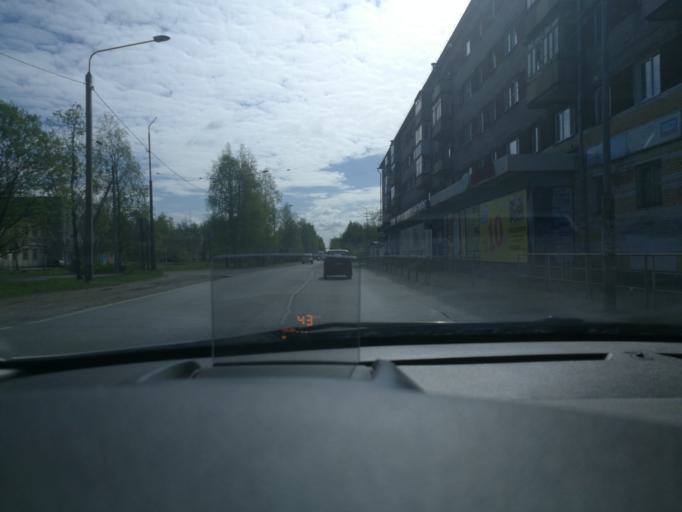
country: RU
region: Arkhangelskaya
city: Arkhangel'sk
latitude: 64.5942
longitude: 40.5803
